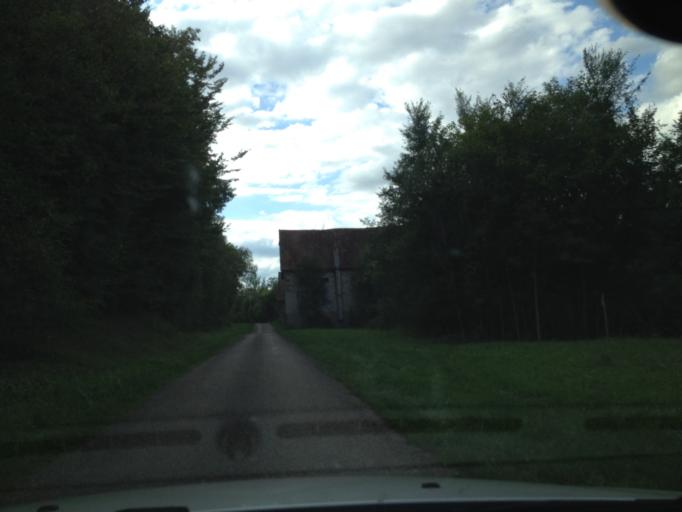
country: FR
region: Franche-Comte
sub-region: Departement de la Haute-Saone
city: Jussey
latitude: 47.8050
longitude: 5.9821
